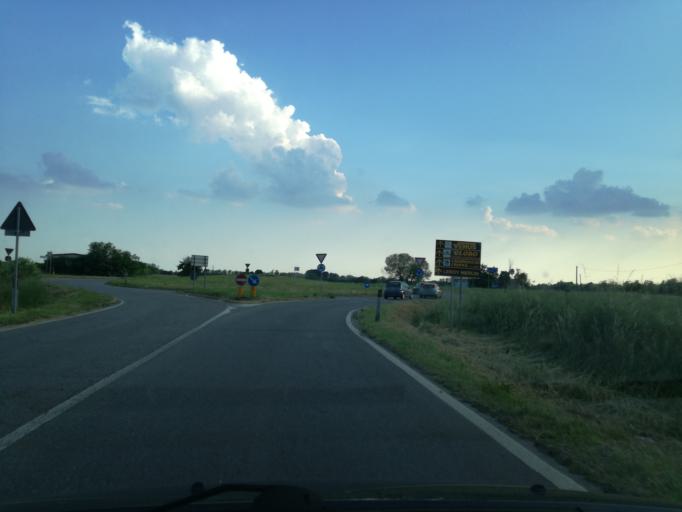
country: IT
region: Lombardy
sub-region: Provincia di Monza e Brianza
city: Cornate d'Adda
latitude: 45.6342
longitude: 9.4619
